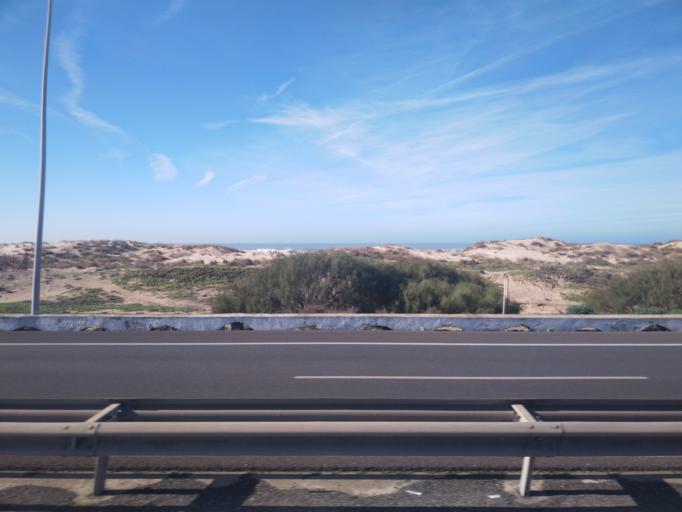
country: ES
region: Andalusia
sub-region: Provincia de Cadiz
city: San Fernando
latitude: 36.4706
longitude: -6.2567
